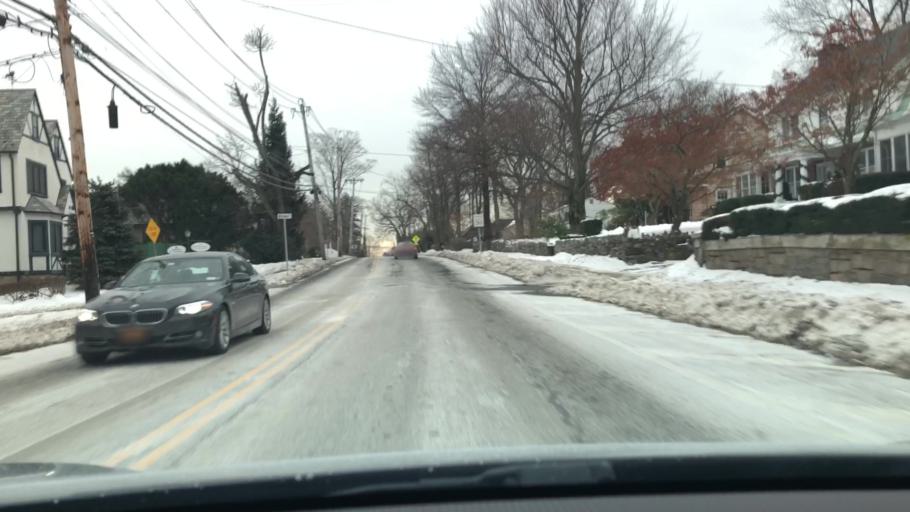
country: US
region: New York
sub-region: Westchester County
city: Harrison
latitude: 40.9743
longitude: -73.7138
